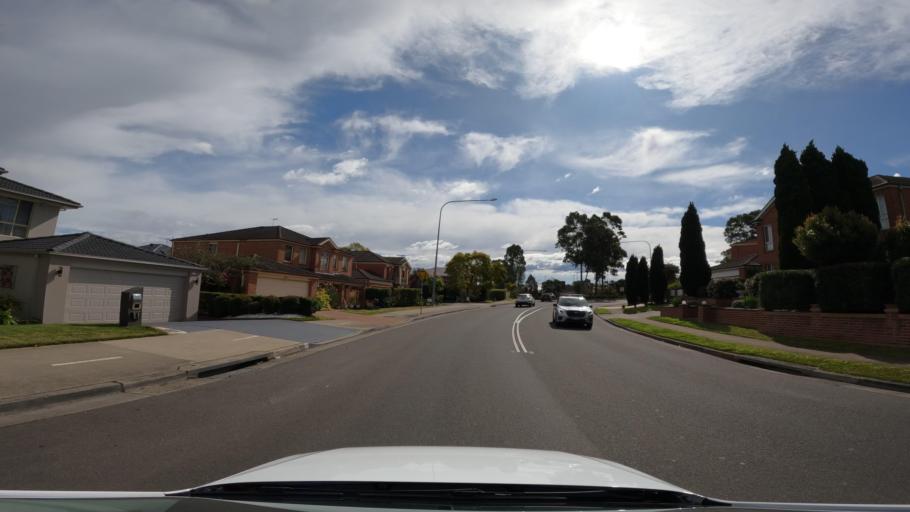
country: AU
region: New South Wales
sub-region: Blacktown
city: Stanhope Gardens
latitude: -33.7264
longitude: 150.9390
